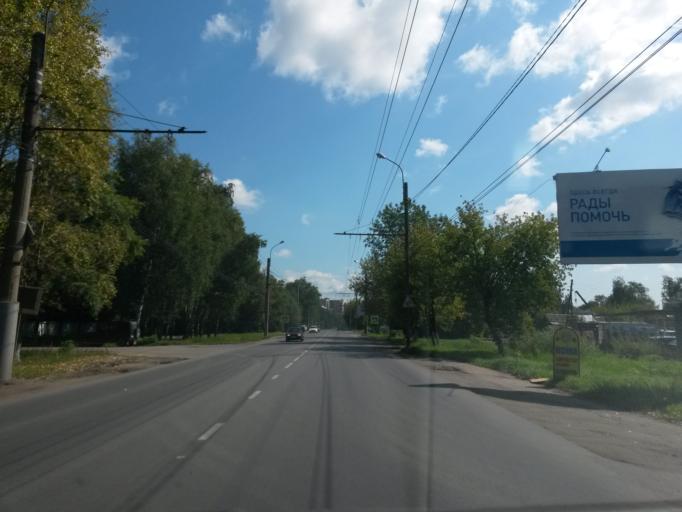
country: RU
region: Ivanovo
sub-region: Gorod Ivanovo
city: Ivanovo
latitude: 56.9996
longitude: 40.9328
